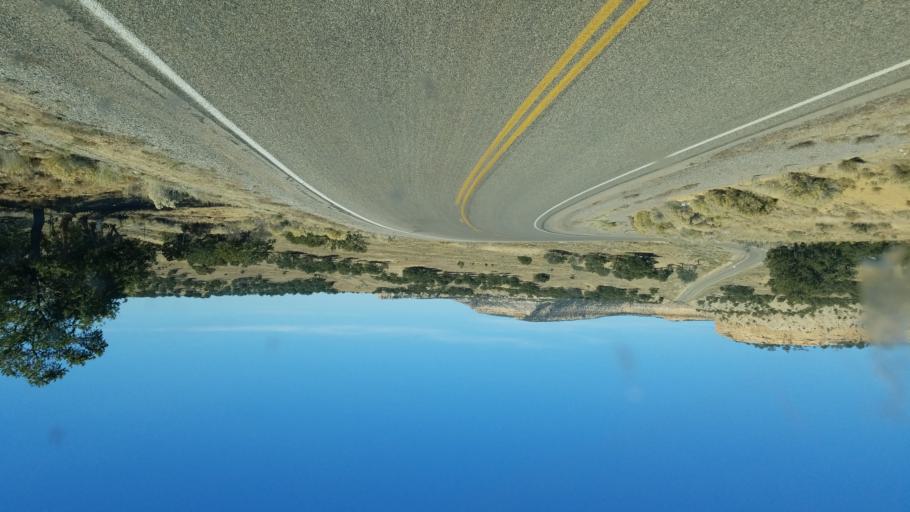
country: US
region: New Mexico
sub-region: McKinley County
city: Crownpoint
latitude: 35.5619
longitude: -108.0995
